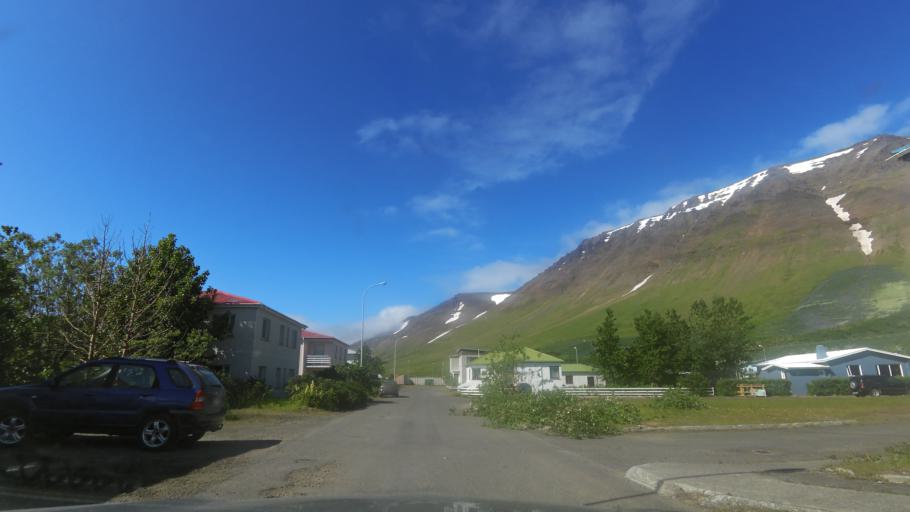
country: IS
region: Westfjords
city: Isafjoerdur
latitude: 66.0510
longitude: -23.5148
